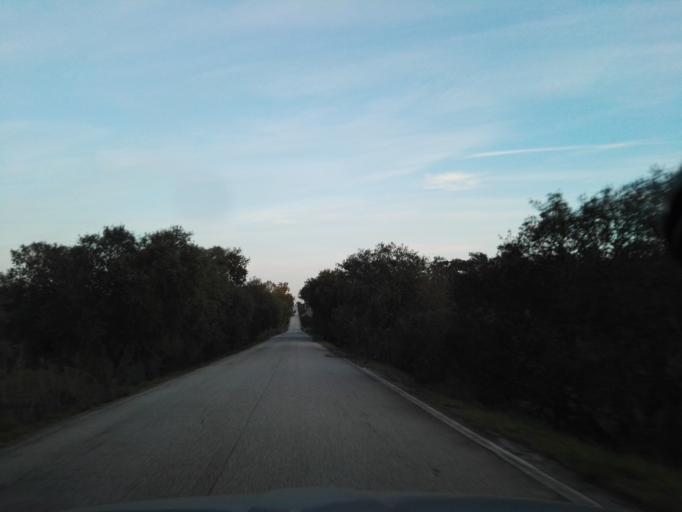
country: PT
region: Evora
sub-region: Montemor-O-Novo
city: Montemor-o-Novo
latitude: 38.7618
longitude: -8.1819
